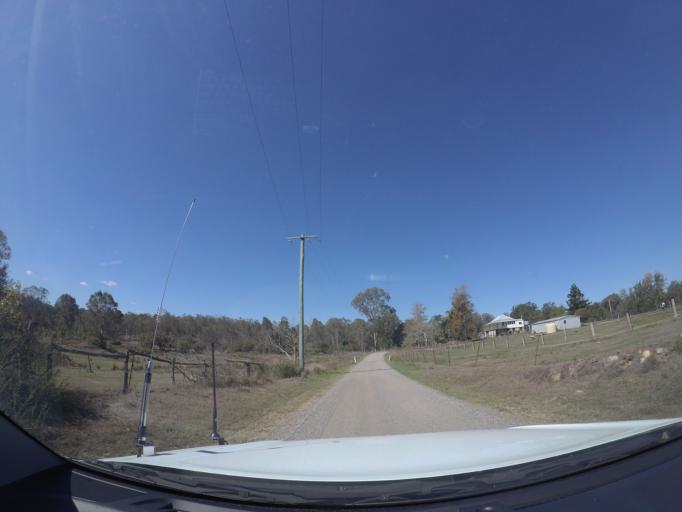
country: AU
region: Queensland
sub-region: Ipswich
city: Springfield Lakes
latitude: -27.7460
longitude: 152.9124
